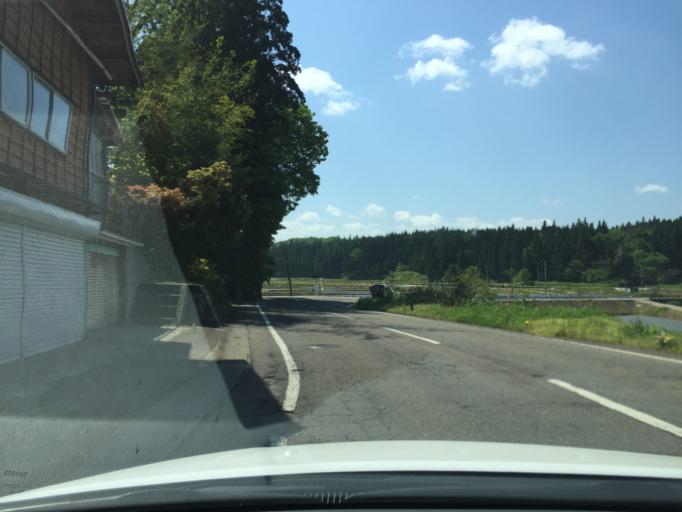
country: JP
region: Niigata
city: Kamo
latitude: 37.5639
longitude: 139.0848
